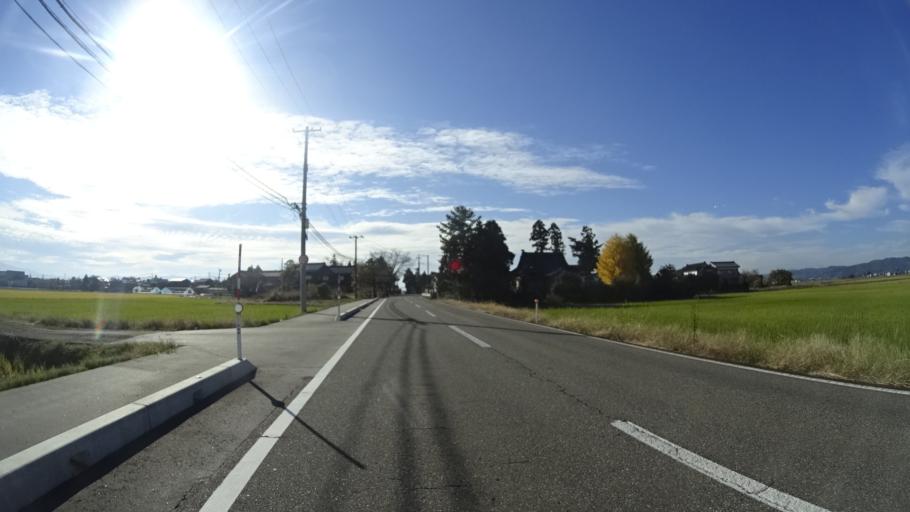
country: JP
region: Niigata
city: Mitsuke
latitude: 37.5594
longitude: 138.8493
